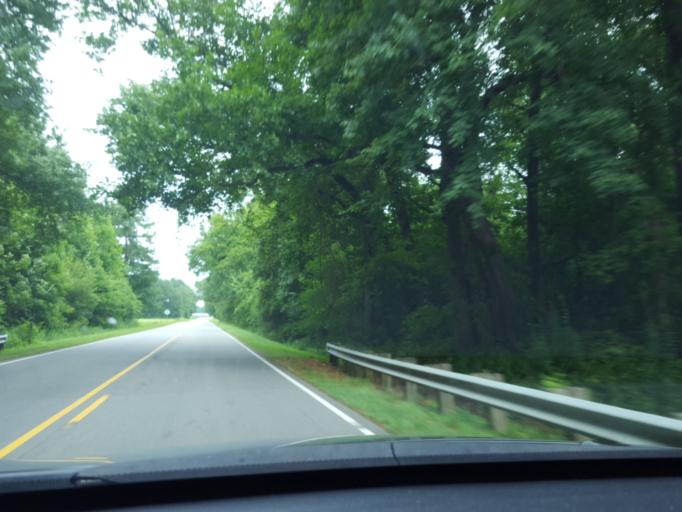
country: US
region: North Carolina
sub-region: Beaufort County
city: Washington
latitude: 35.6923
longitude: -76.9897
